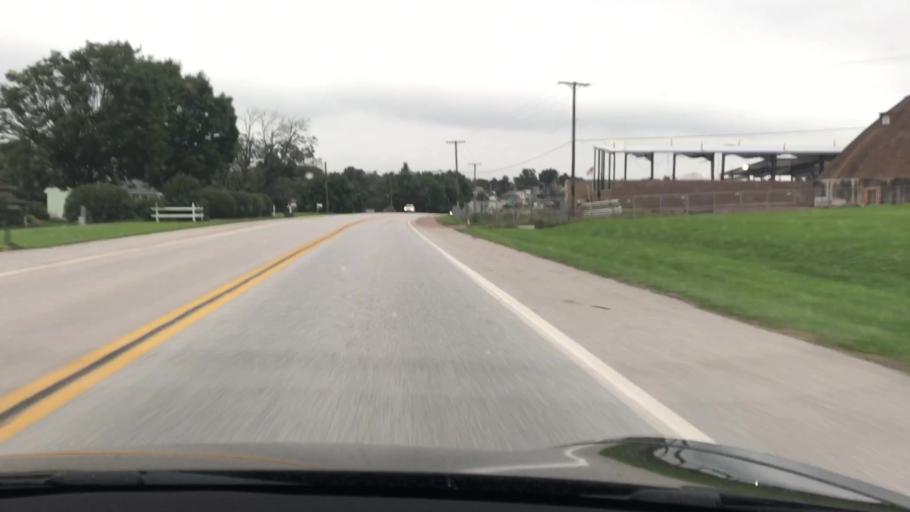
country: US
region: Pennsylvania
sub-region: York County
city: Dover
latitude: 39.9953
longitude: -76.8562
